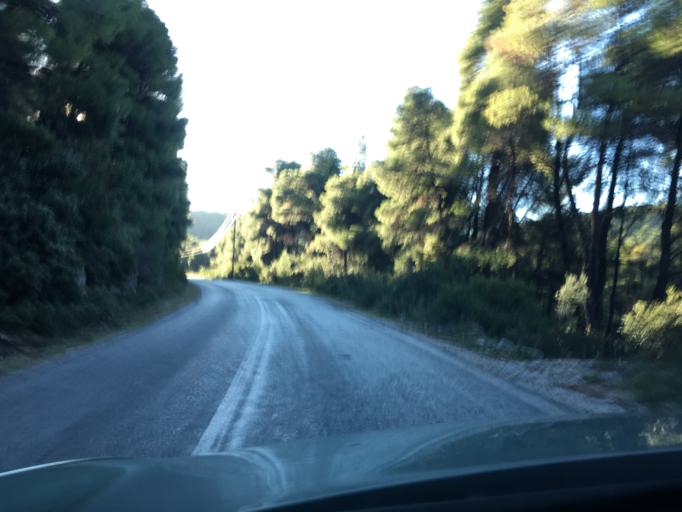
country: GR
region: Thessaly
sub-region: Nomos Magnisias
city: Skopelos
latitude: 39.1055
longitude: 23.6634
